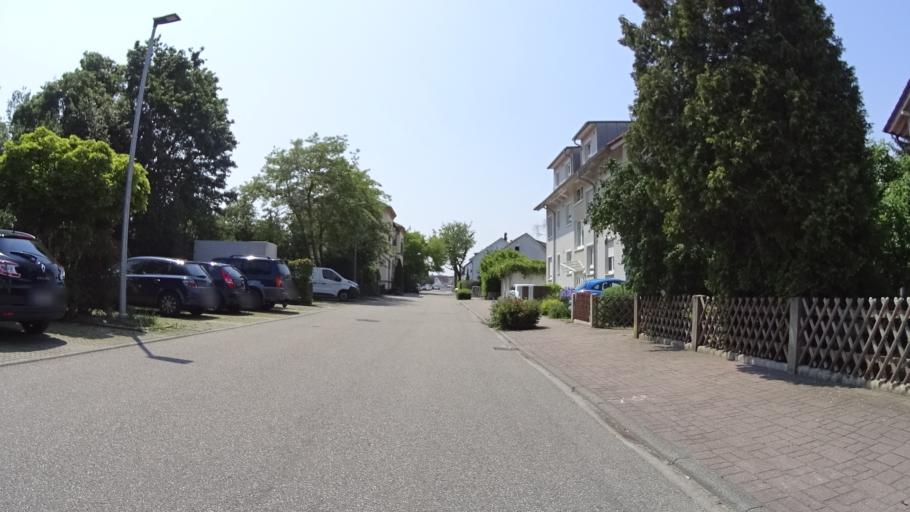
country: DE
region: Baden-Wuerttemberg
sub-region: Karlsruhe Region
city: Eggenstein-Leopoldshafen
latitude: 49.0750
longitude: 8.3973
